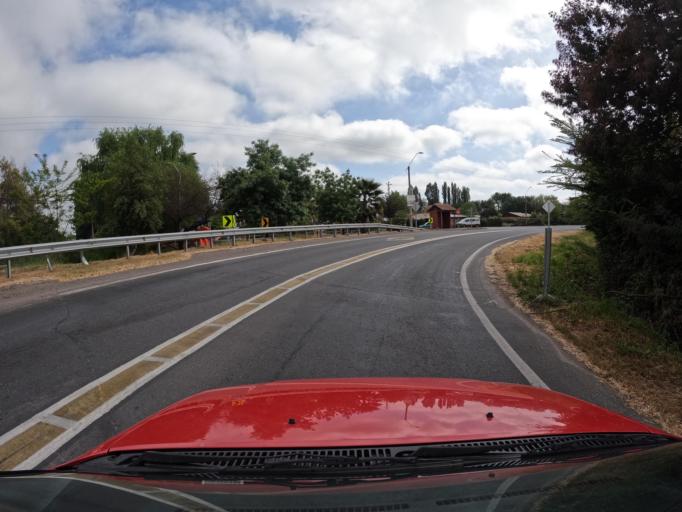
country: CL
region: O'Higgins
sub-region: Provincia de Colchagua
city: Santa Cruz
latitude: -34.6739
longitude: -71.3495
